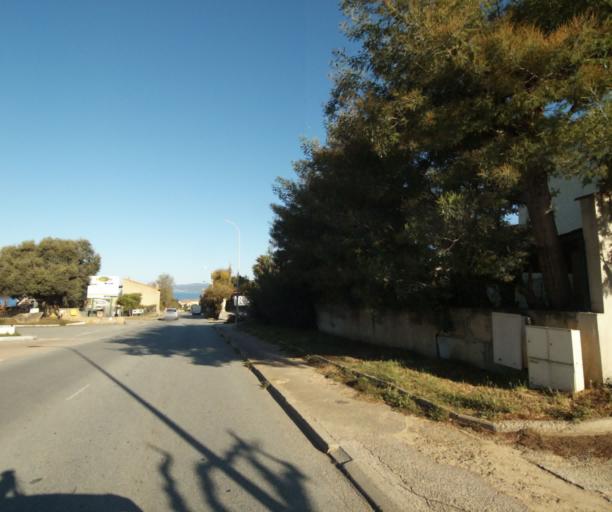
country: FR
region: Corsica
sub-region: Departement de la Corse-du-Sud
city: Propriano
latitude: 41.6708
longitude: 8.9132
